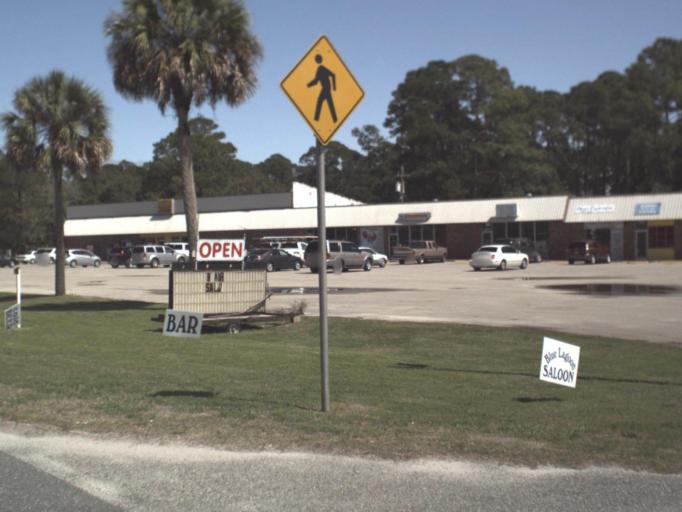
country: US
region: Florida
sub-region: Wakulla County
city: Crawfordville
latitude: 30.0282
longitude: -84.3903
